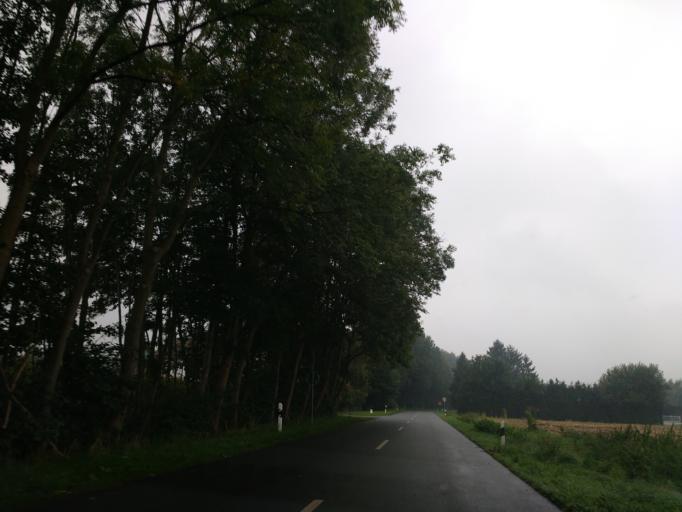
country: DE
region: North Rhine-Westphalia
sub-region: Regierungsbezirk Detmold
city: Delbruck
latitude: 51.7709
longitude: 8.4972
